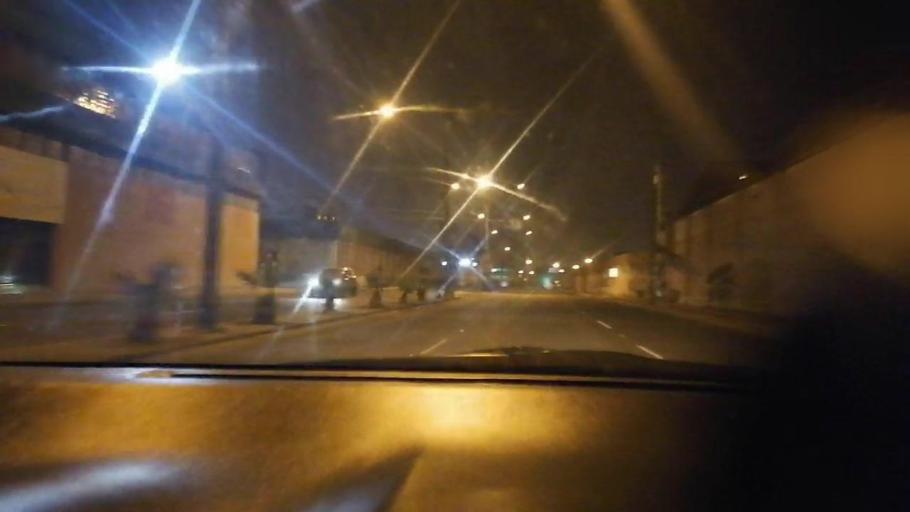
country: PE
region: Callao
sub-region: Callao
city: Callao
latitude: -12.0437
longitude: -77.0770
